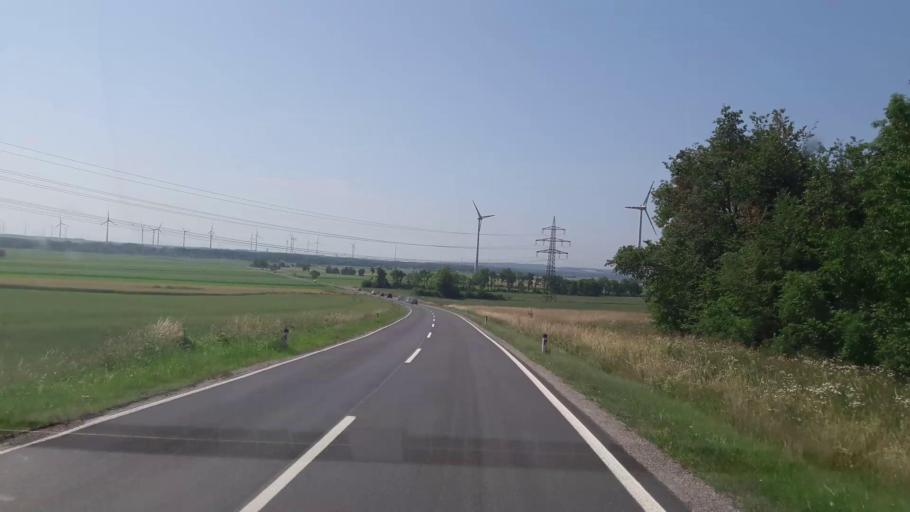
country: AT
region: Lower Austria
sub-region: Politischer Bezirk Bruck an der Leitha
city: Petronell-Carnuntum
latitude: 48.0969
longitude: 16.8626
